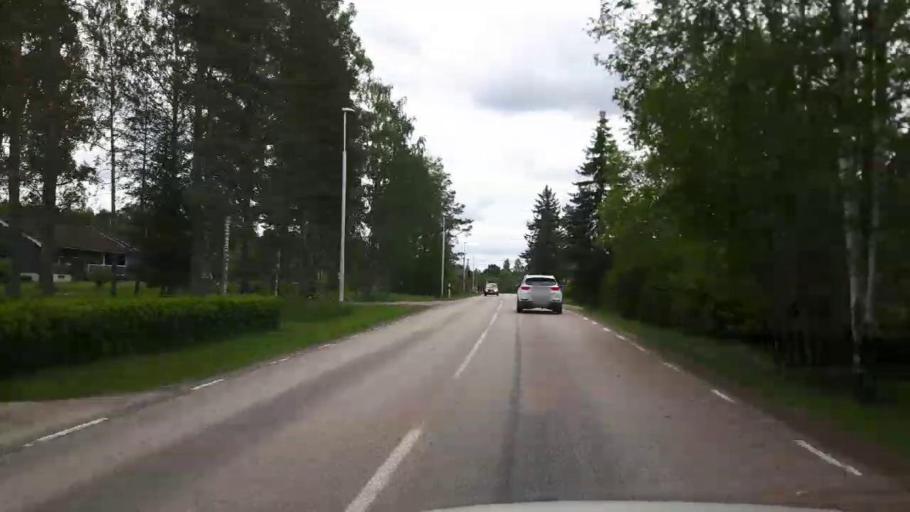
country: SE
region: Vaestmanland
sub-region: Norbergs Kommun
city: Norberg
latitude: 60.1041
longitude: 15.9251
